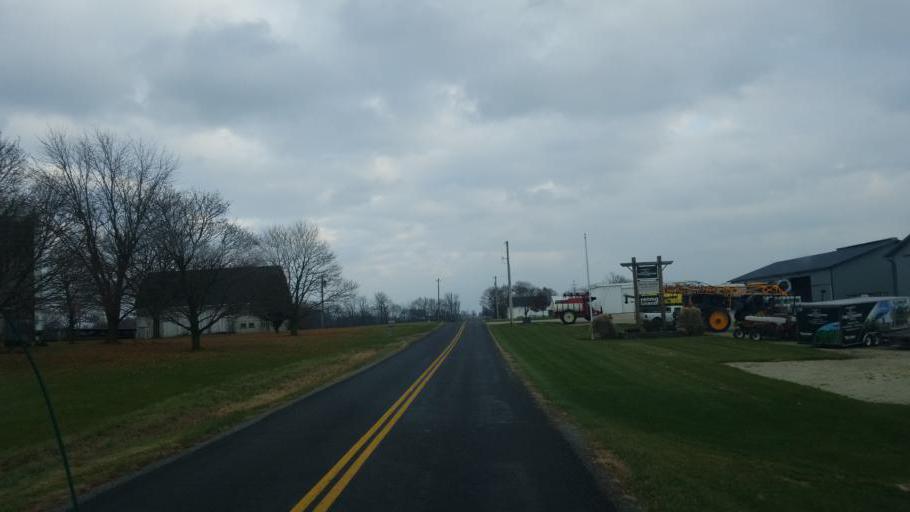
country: US
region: Ohio
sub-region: Mercer County
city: Fort Recovery
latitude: 40.5090
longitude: -84.7498
